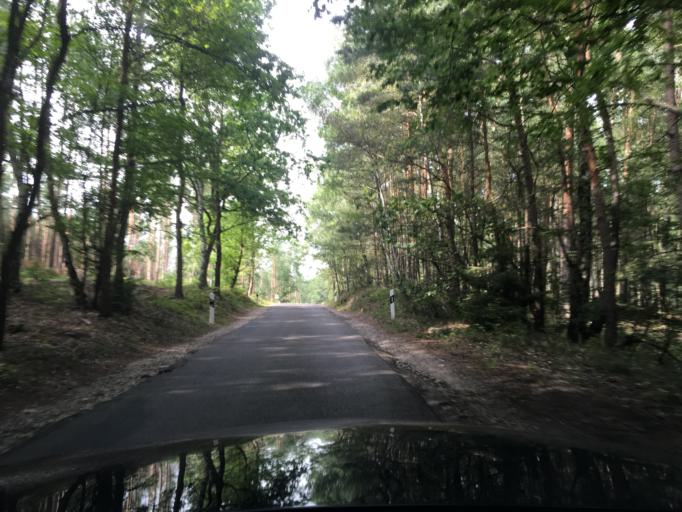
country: DE
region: Mecklenburg-Vorpommern
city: Mollenhagen
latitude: 53.4515
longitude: 12.8203
